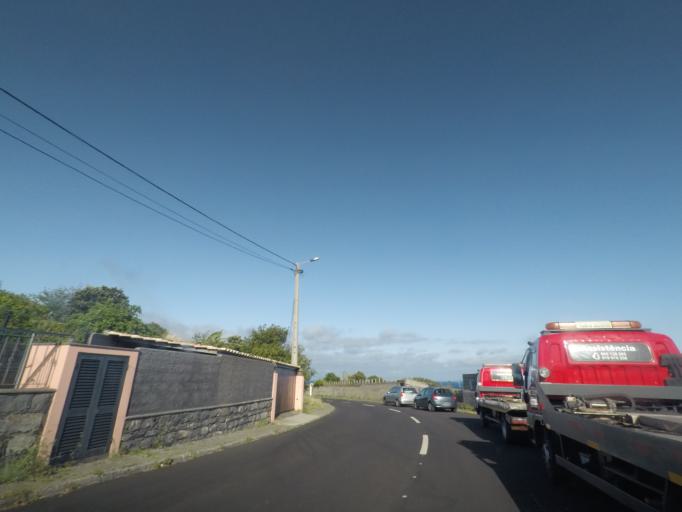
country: PT
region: Madeira
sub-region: Santa Cruz
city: Santa Cruz
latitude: 32.6902
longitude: -16.7870
